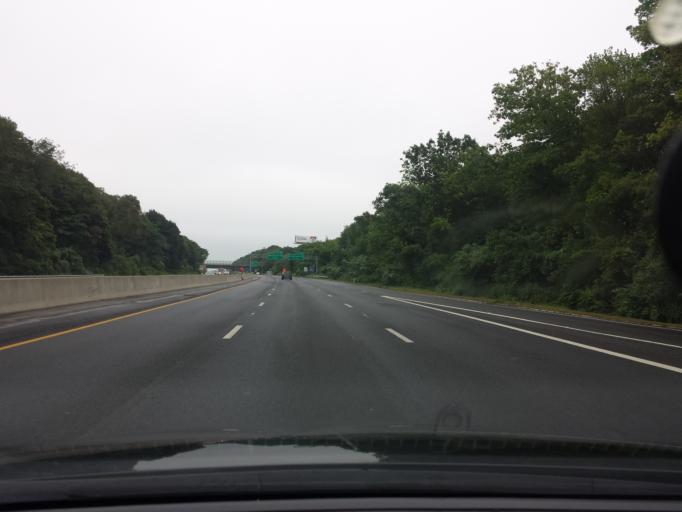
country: US
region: Massachusetts
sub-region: Bristol County
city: New Bedford
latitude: 41.6520
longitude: -70.9488
